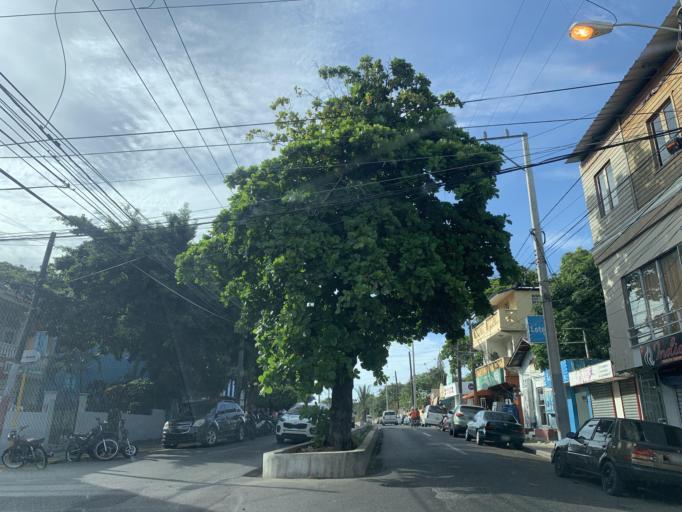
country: DO
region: Puerto Plata
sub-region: Puerto Plata
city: Puerto Plata
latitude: 19.7926
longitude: -70.6827
